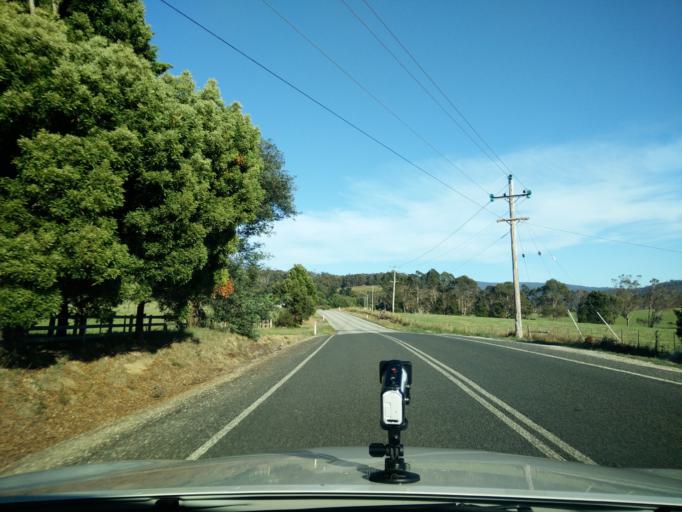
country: AU
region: Tasmania
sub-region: Break O'Day
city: St Helens
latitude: -41.2693
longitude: 148.0965
